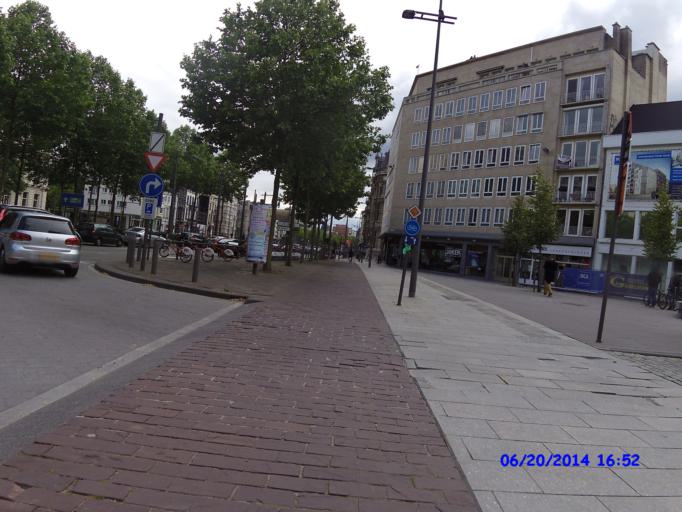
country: BE
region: Flanders
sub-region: Provincie Antwerpen
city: Antwerpen
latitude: 51.2128
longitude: 4.4095
